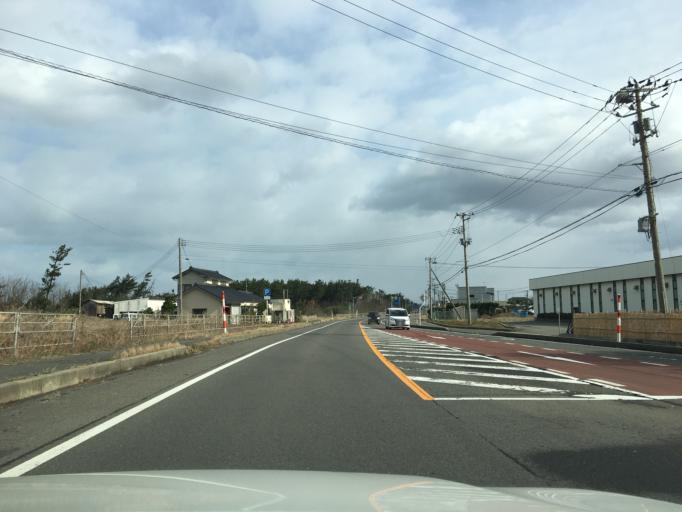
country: JP
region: Yamagata
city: Yuza
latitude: 39.2362
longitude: 139.9105
